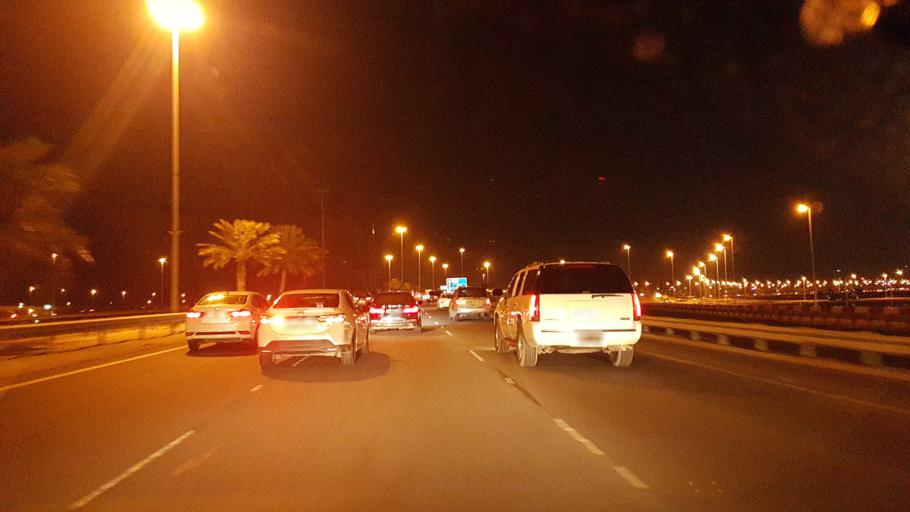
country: BH
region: Northern
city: Madinat `Isa
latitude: 26.1801
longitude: 50.5026
